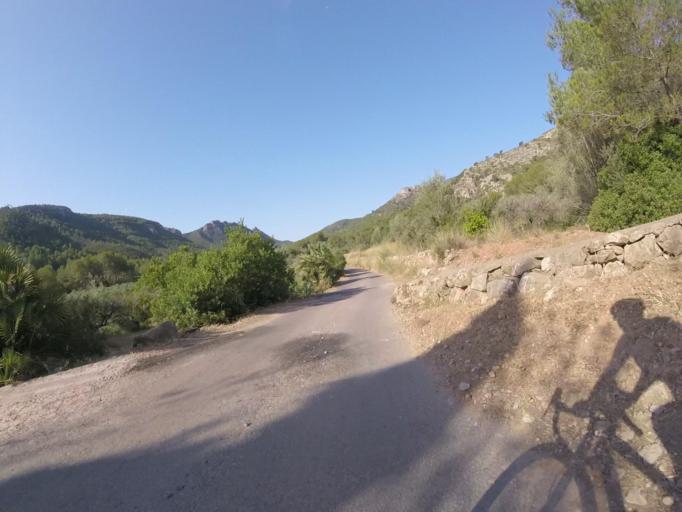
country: ES
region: Valencia
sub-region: Provincia de Castello
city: Benicassim
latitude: 40.1004
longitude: 0.0646
